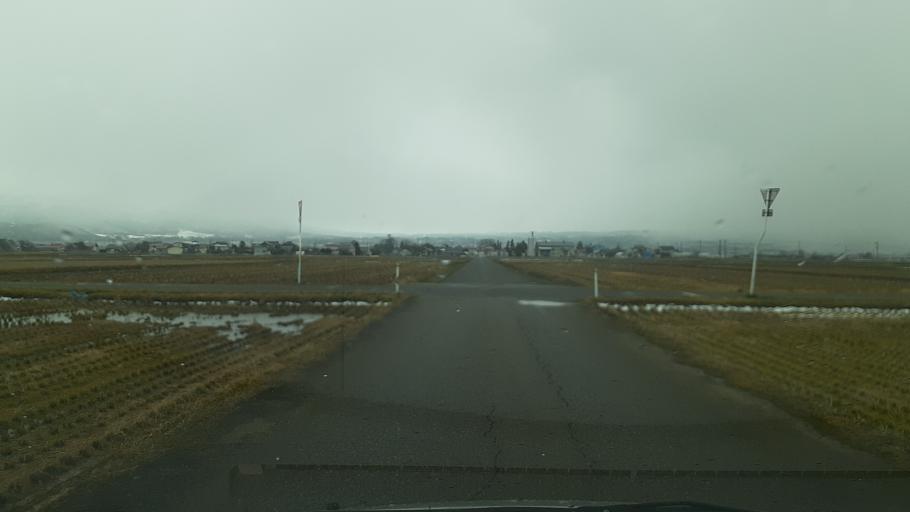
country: JP
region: Fukushima
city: Kitakata
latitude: 37.5603
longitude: 139.8779
